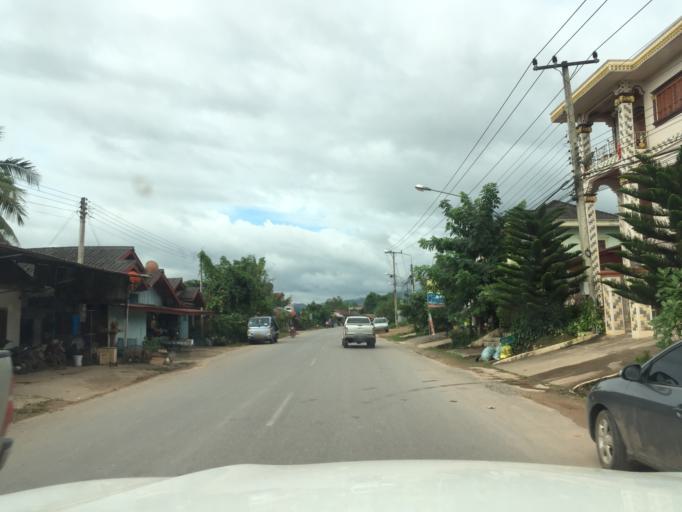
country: LA
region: Oudomxai
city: Muang Xay
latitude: 20.6991
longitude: 101.9914
